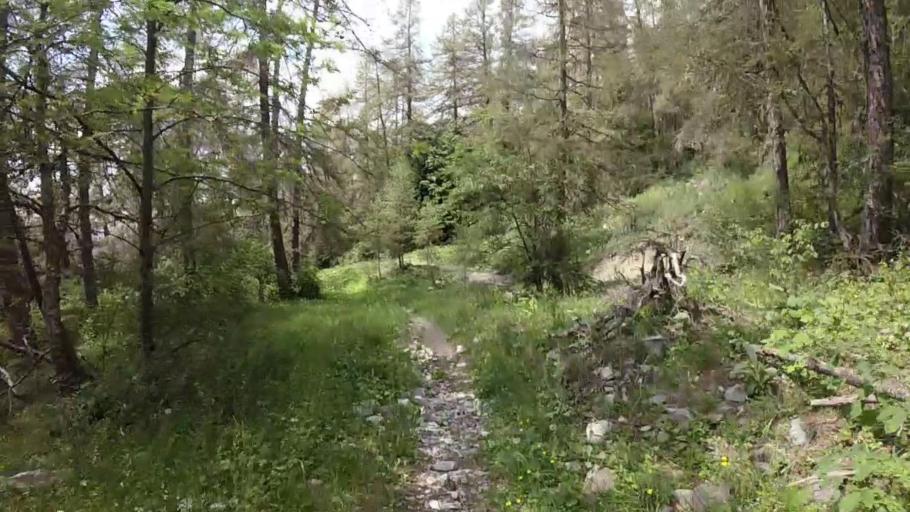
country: FR
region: Provence-Alpes-Cote d'Azur
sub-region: Departement des Alpes-de-Haute-Provence
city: Seyne-les-Alpes
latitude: 44.4087
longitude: 6.3680
